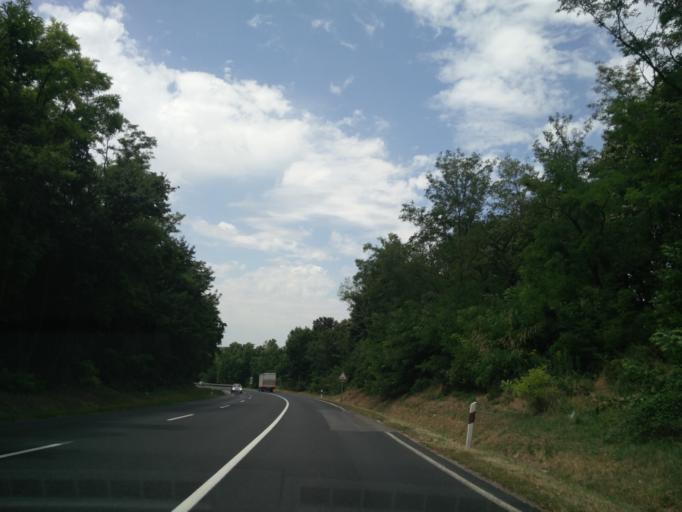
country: HU
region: Veszprem
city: Ajka
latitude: 47.1430
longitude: 17.5671
